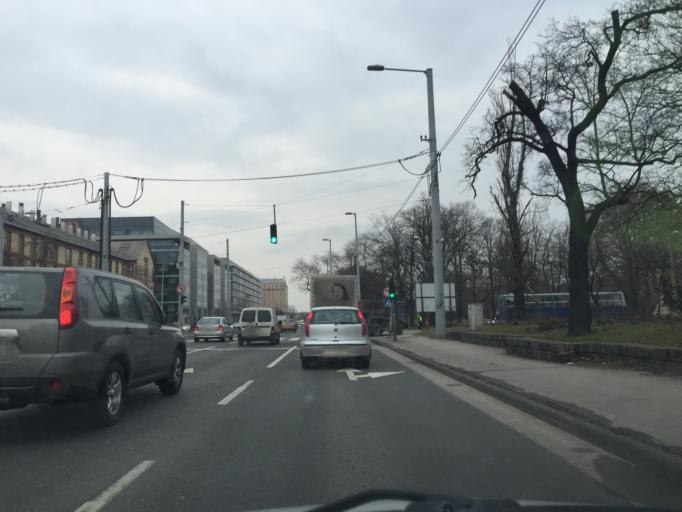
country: HU
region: Budapest
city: Budapest VIII. keruelet
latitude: 47.4778
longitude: 19.1005
